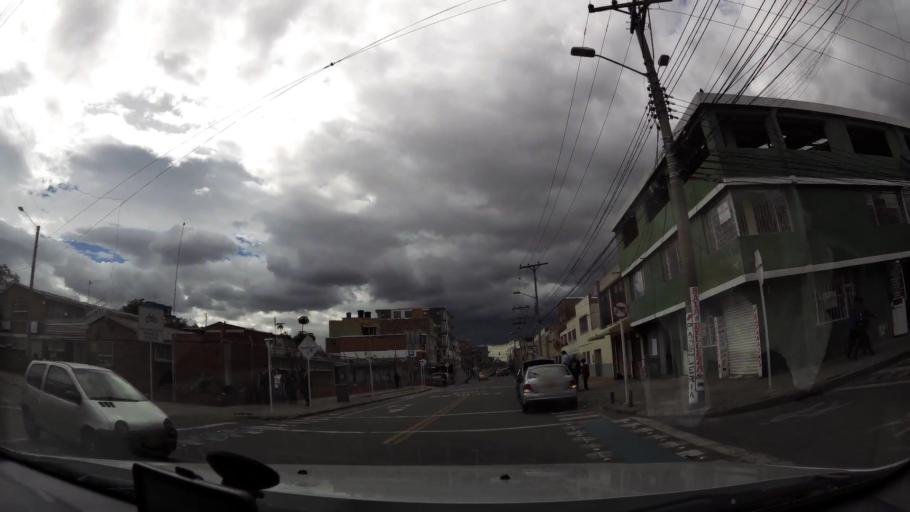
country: CO
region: Bogota D.C.
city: Bogota
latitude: 4.6021
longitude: -74.1292
